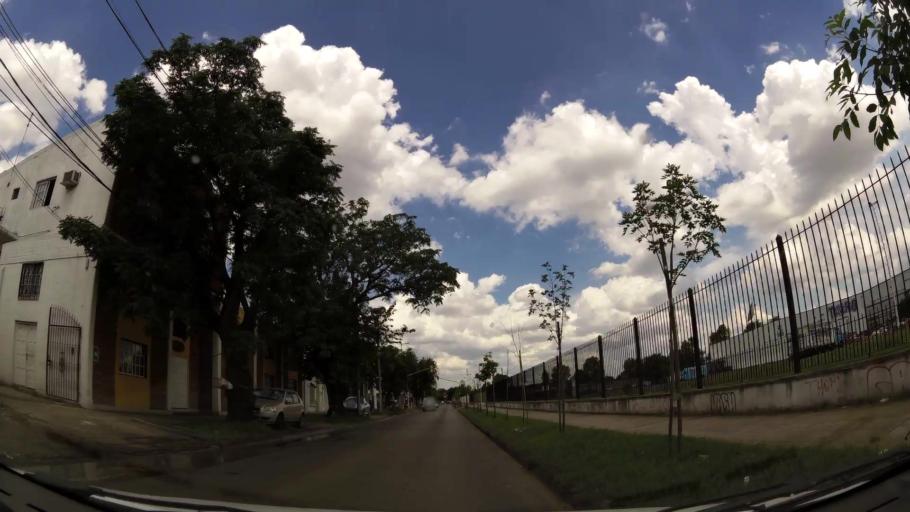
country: AR
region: Buenos Aires
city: Ituzaingo
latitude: -34.6475
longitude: -58.6795
